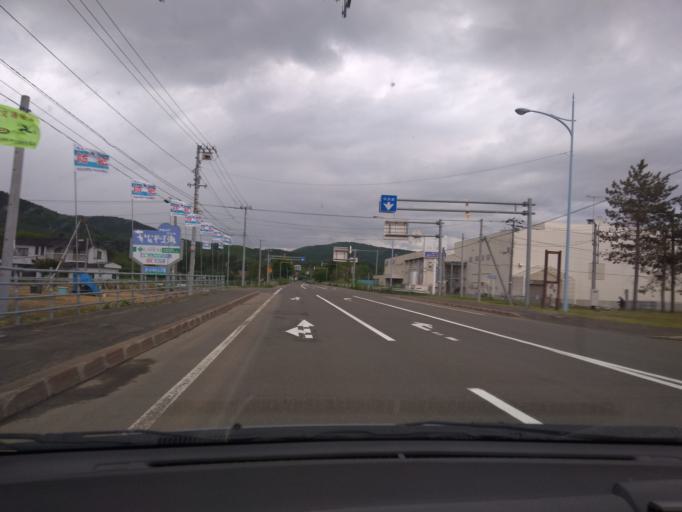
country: JP
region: Hokkaido
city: Shimo-furano
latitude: 43.1699
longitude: 142.5717
